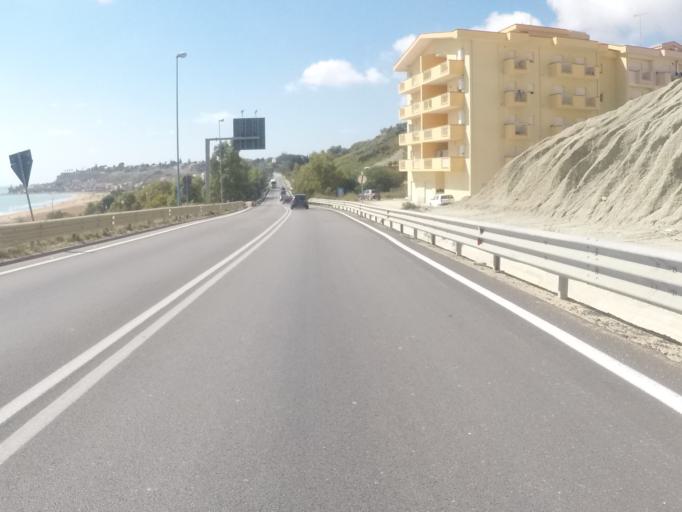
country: IT
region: Sicily
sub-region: Agrigento
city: Porto Empedocle
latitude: 37.2933
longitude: 13.5115
